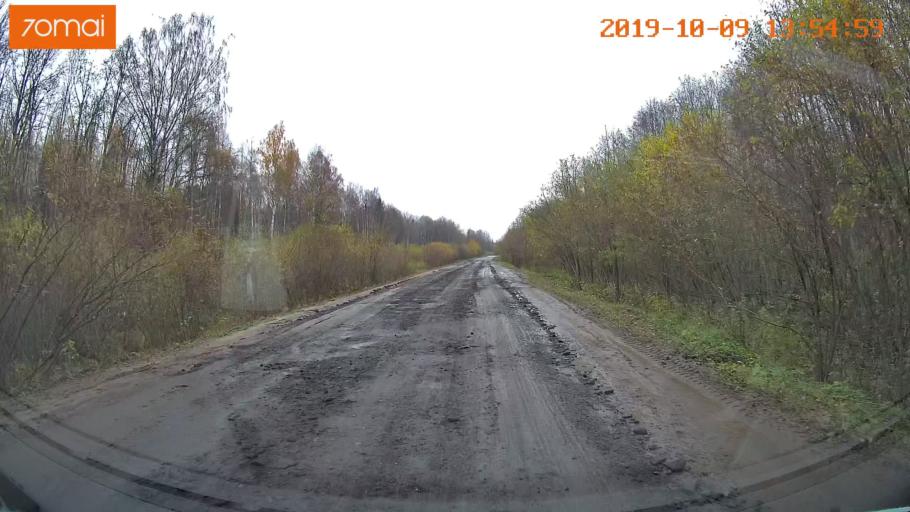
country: RU
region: Kostroma
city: Buy
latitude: 58.4226
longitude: 41.2701
